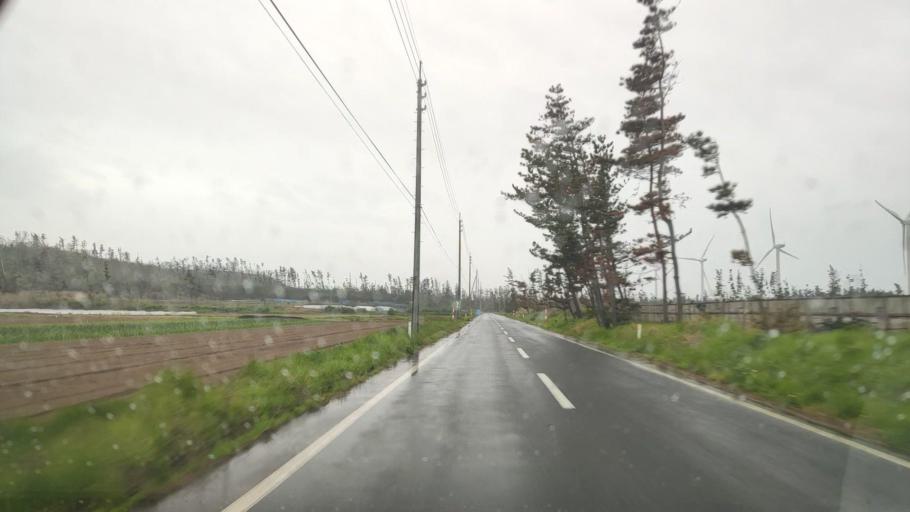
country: JP
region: Akita
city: Noshiromachi
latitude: 40.0838
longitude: 139.9568
